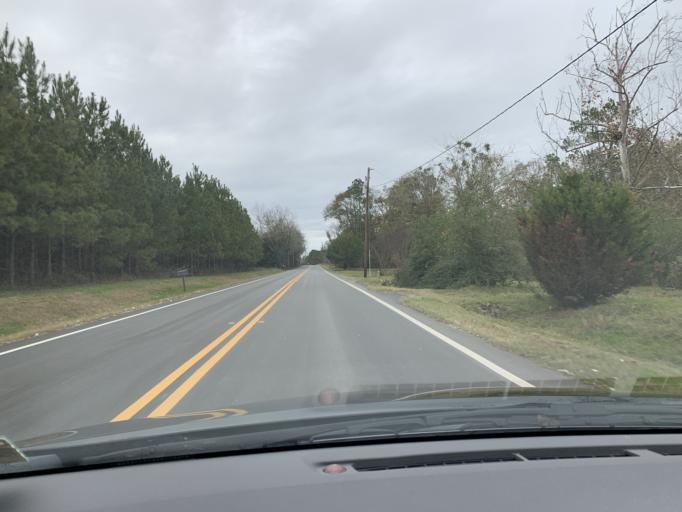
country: US
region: Georgia
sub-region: Thomas County
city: Meigs
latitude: 31.0077
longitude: -84.0617
